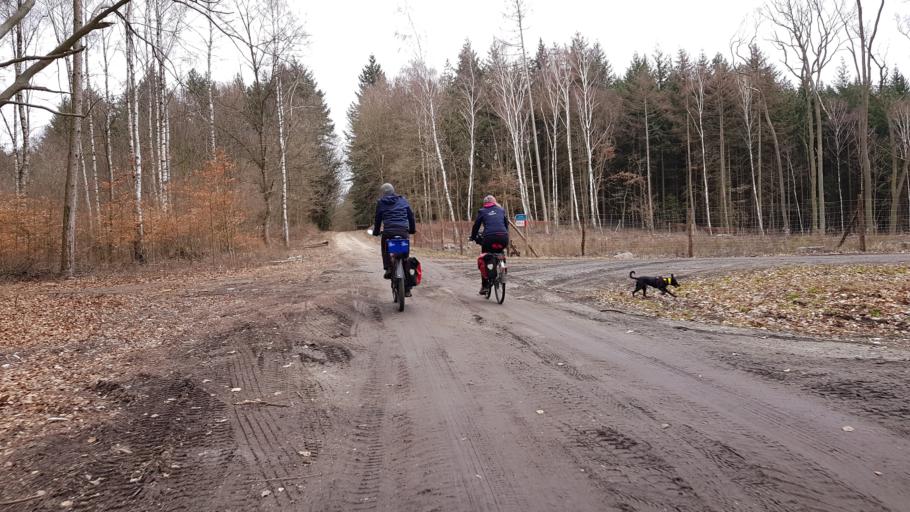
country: PL
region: West Pomeranian Voivodeship
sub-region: Powiat gryfinski
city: Banie
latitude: 53.0689
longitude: 14.7388
